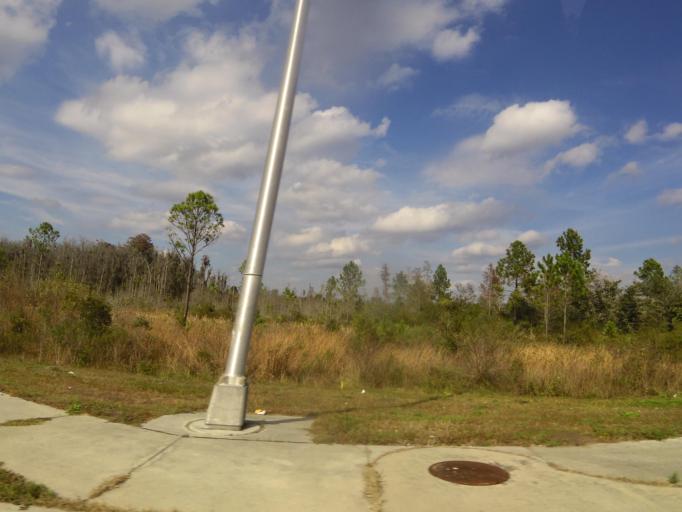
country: US
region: Florida
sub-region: Duval County
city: Baldwin
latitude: 30.2761
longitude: -81.8790
